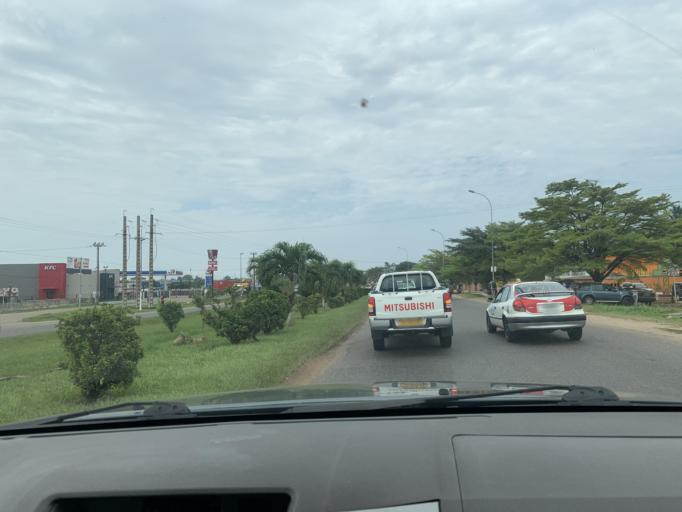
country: GA
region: Estuaire
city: Libreville
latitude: 0.3399
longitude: 9.4773
